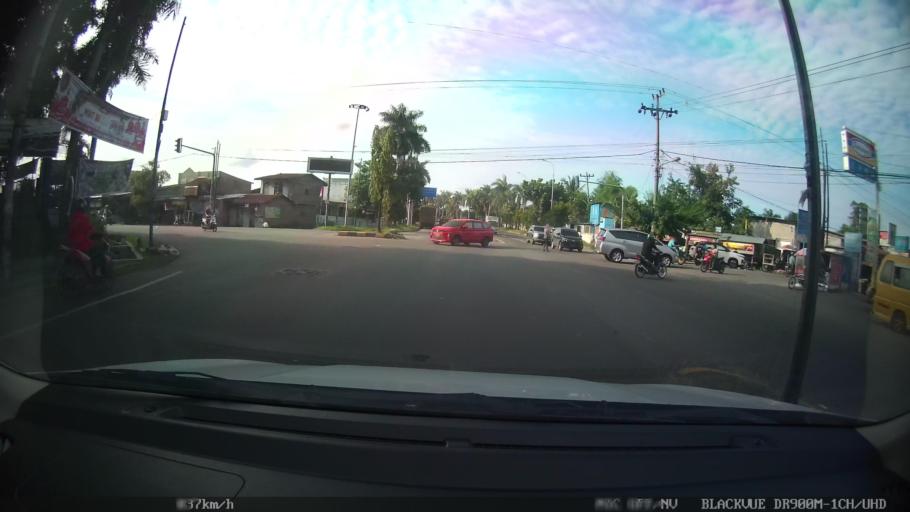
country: ID
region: North Sumatra
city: Medan
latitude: 3.6418
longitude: 98.6813
